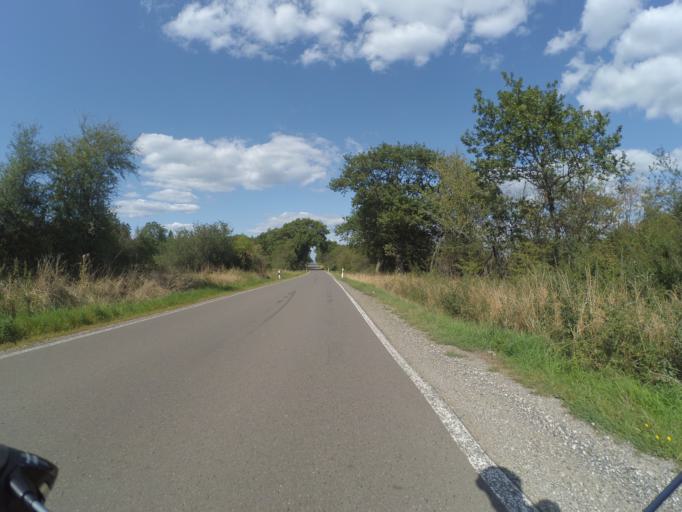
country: DE
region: Rheinland-Pfalz
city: Polich
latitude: 49.7728
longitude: 6.8468
